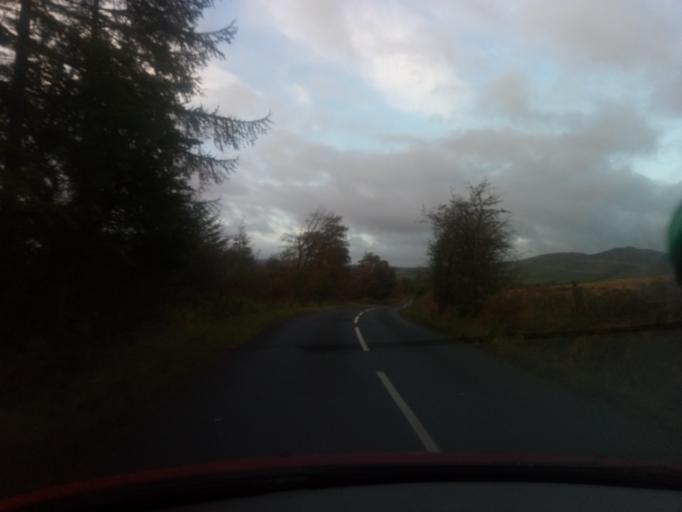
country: GB
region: Scotland
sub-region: The Scottish Borders
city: Jedburgh
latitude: 55.4347
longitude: -2.6026
